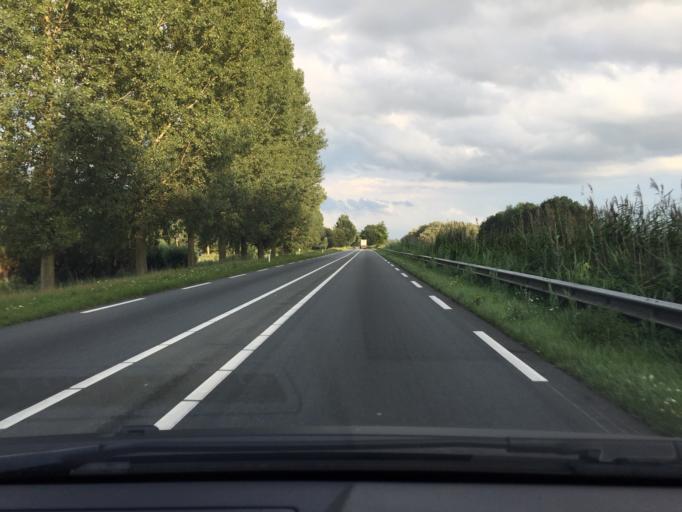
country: NL
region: North Brabant
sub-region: Gemeente Veghel
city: Zijtaart
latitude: 51.5939
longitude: 5.5595
